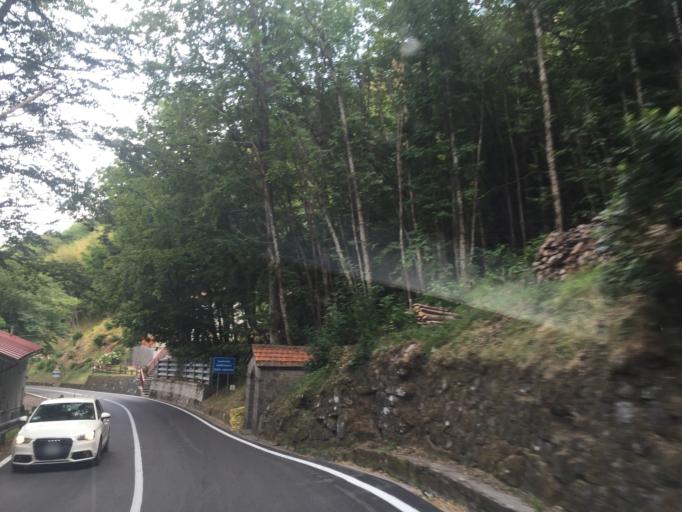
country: IT
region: Tuscany
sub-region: Provincia di Pistoia
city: Cutigliano
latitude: 44.1186
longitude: 10.7299
